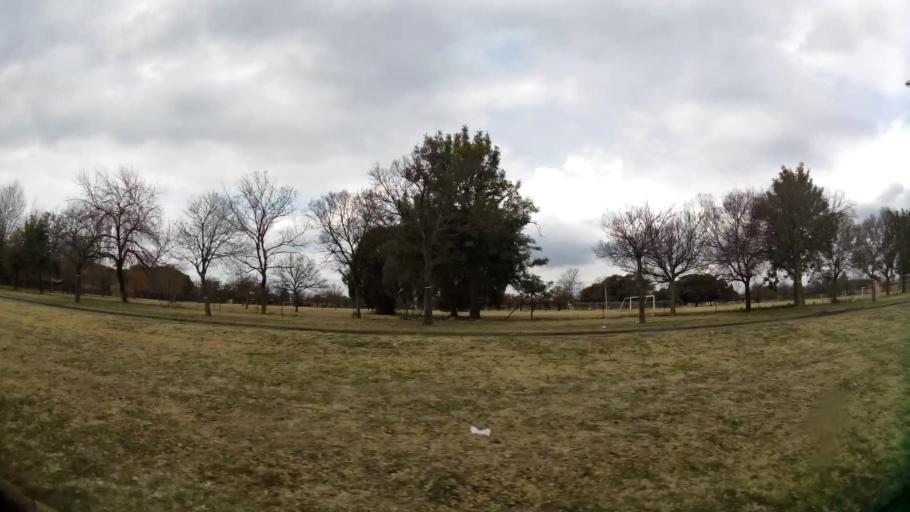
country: ZA
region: Gauteng
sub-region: Sedibeng District Municipality
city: Vanderbijlpark
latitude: -26.7150
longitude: 27.8235
